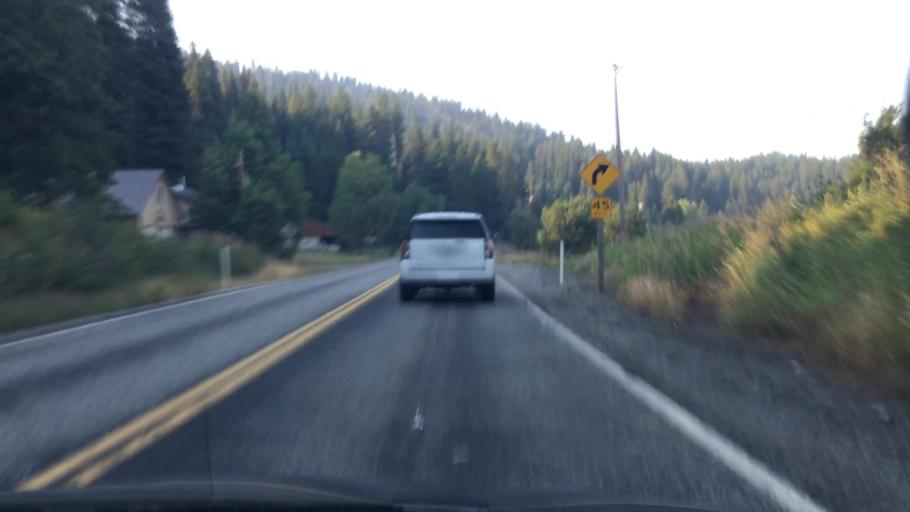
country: US
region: Idaho
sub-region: Valley County
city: Cascade
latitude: 44.3060
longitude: -116.0875
